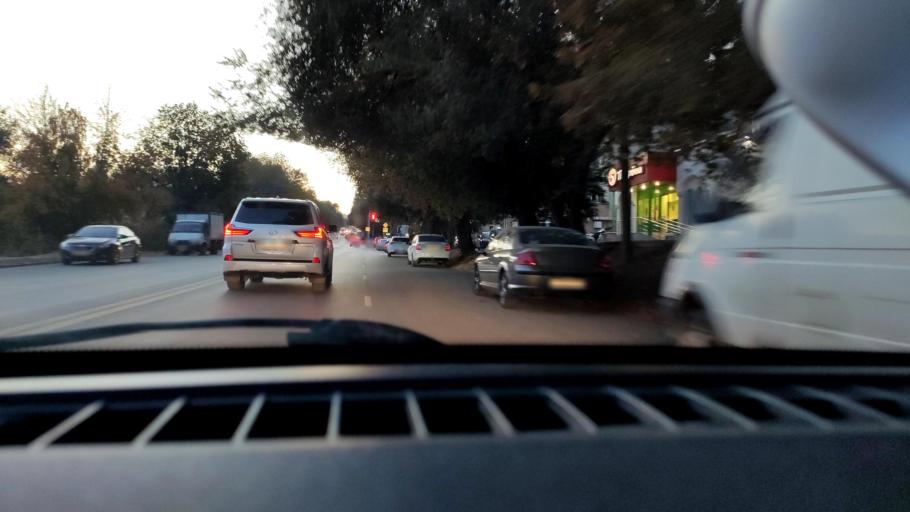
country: RU
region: Samara
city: Samara
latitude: 53.2067
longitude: 50.2231
